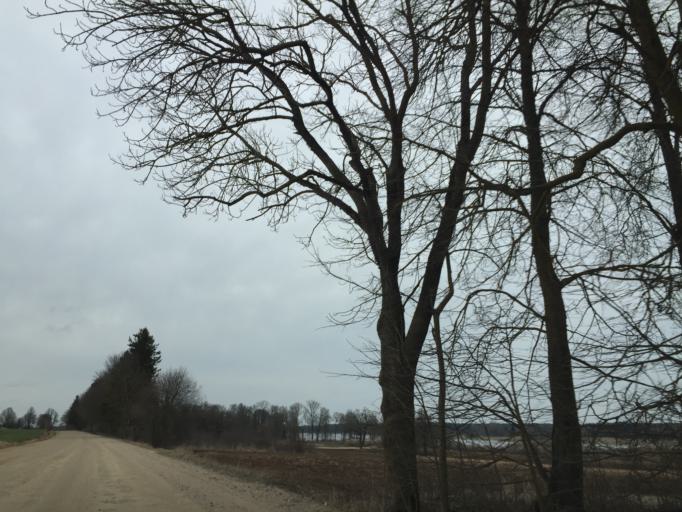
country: LV
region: Livani
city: Livani
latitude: 56.2910
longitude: 26.1759
